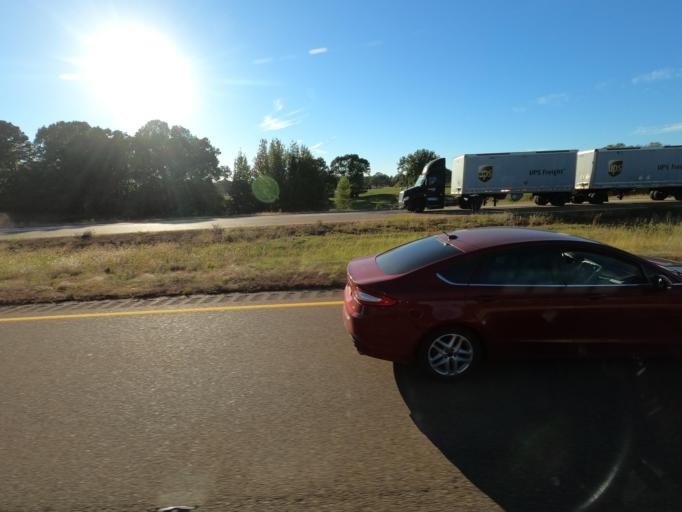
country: US
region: Tennessee
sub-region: Fayette County
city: Hickory Withe
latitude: 35.1524
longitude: -89.6381
